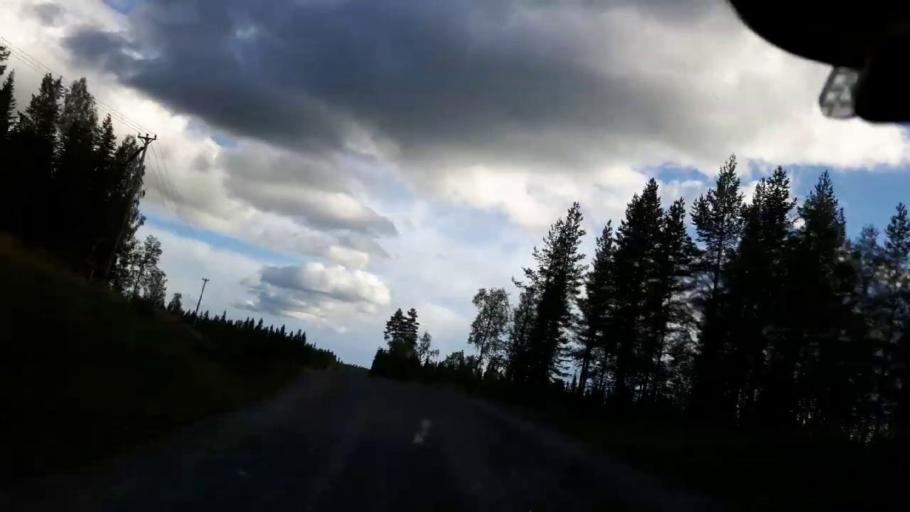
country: SE
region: Jaemtland
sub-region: Stroemsunds Kommun
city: Stroemsund
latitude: 63.3213
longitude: 15.5839
